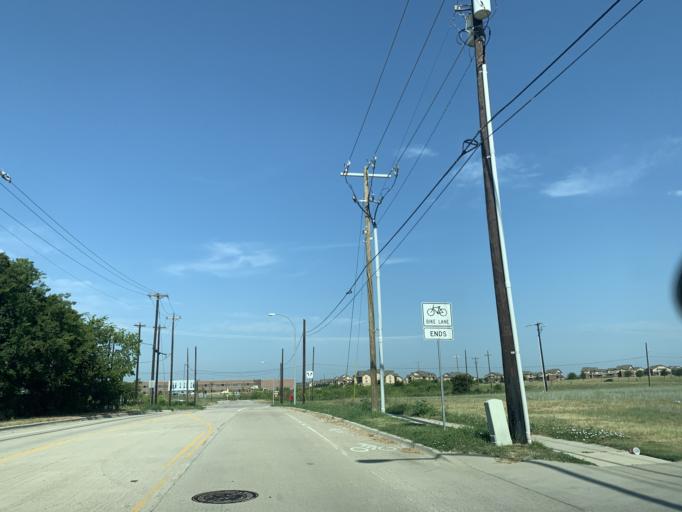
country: US
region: Texas
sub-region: Tarrant County
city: Blue Mound
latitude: 32.8908
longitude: -97.3054
